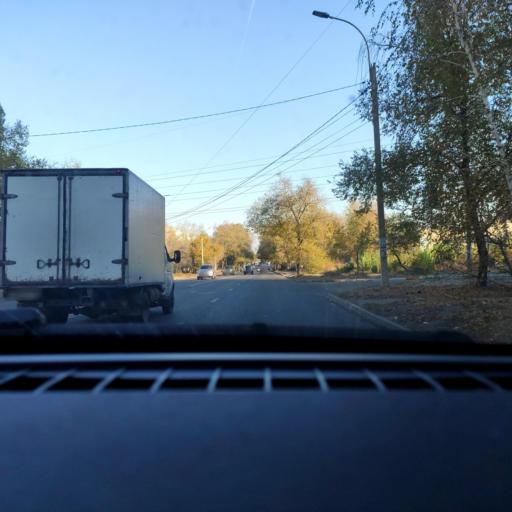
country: RU
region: Voronezj
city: Maslovka
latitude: 51.5975
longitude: 39.2438
